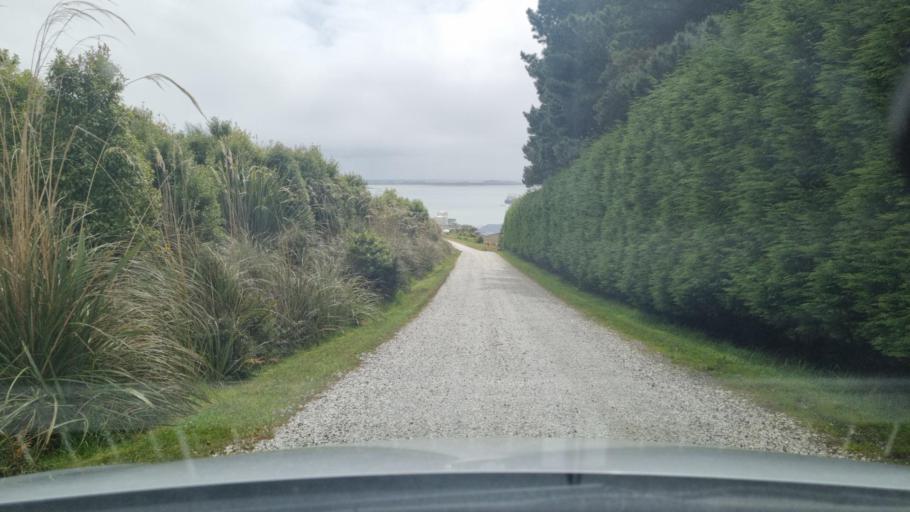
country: NZ
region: Southland
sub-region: Invercargill City
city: Bluff
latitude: -46.6100
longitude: 168.3521
